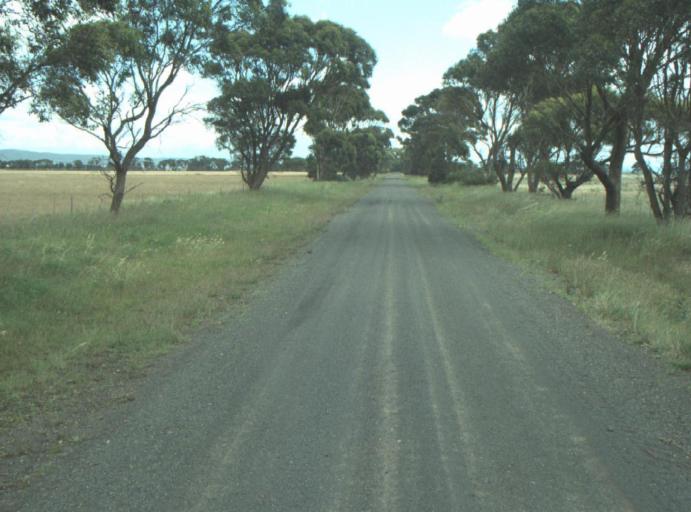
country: AU
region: Victoria
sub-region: Greater Geelong
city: Lara
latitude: -37.8790
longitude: 144.3501
